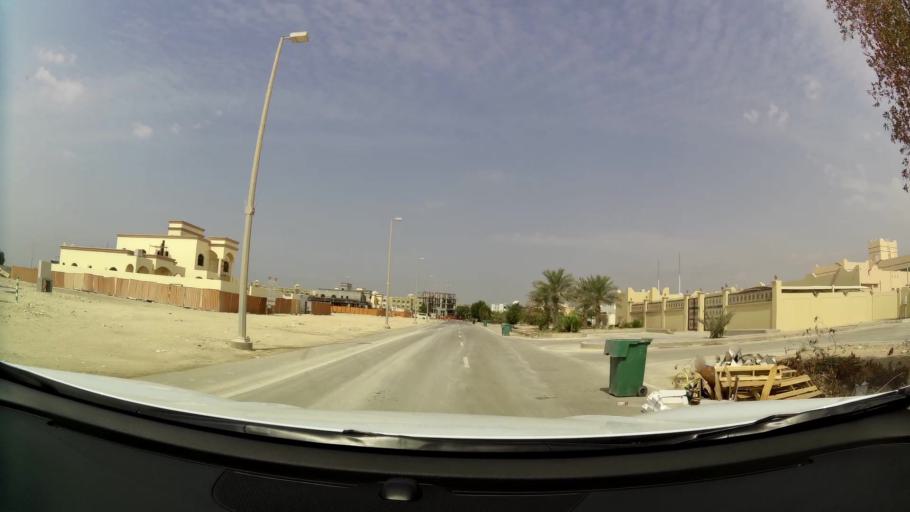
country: AE
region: Abu Dhabi
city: Abu Dhabi
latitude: 24.5279
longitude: 54.6813
